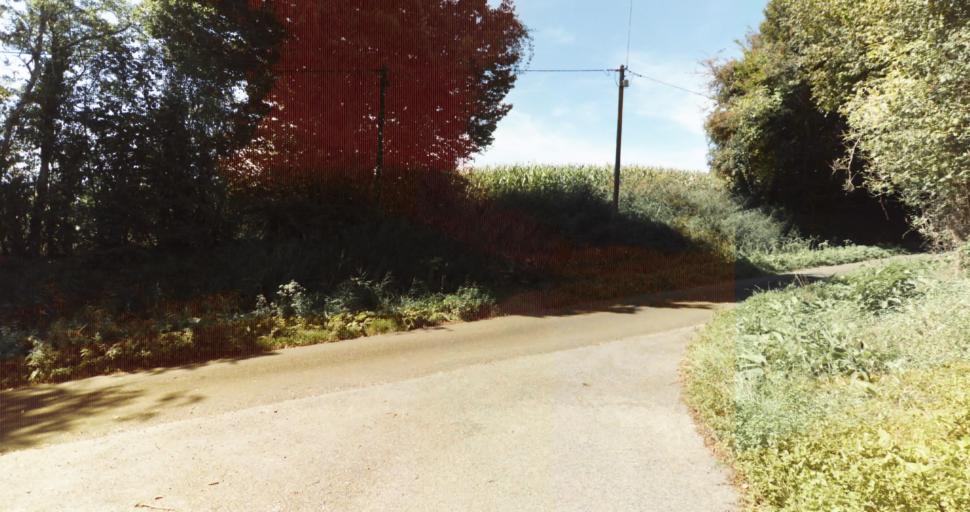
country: FR
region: Lower Normandy
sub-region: Departement de l'Orne
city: Gace
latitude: 48.7602
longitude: 0.2690
